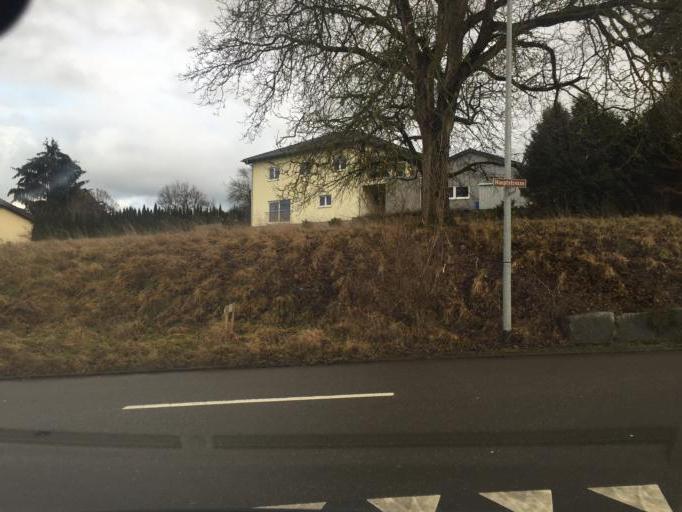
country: DE
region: Baden-Wuerttemberg
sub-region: Freiburg Region
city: Busingen
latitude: 47.6568
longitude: 8.6990
